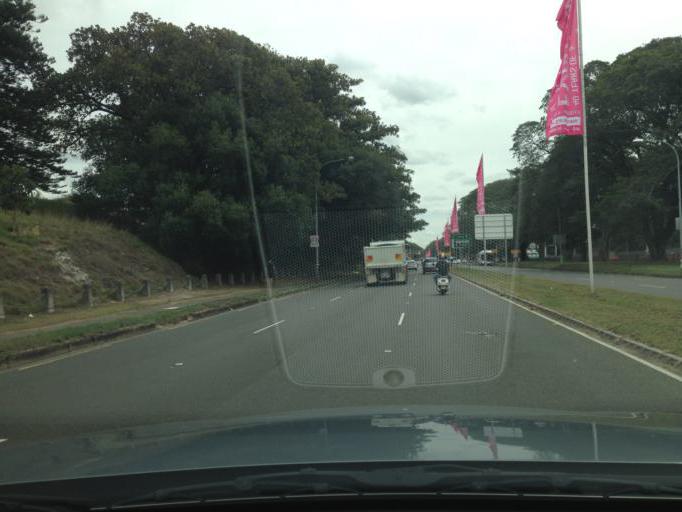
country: AU
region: New South Wales
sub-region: Woollahra
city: Paddington
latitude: -33.8981
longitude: 151.2220
